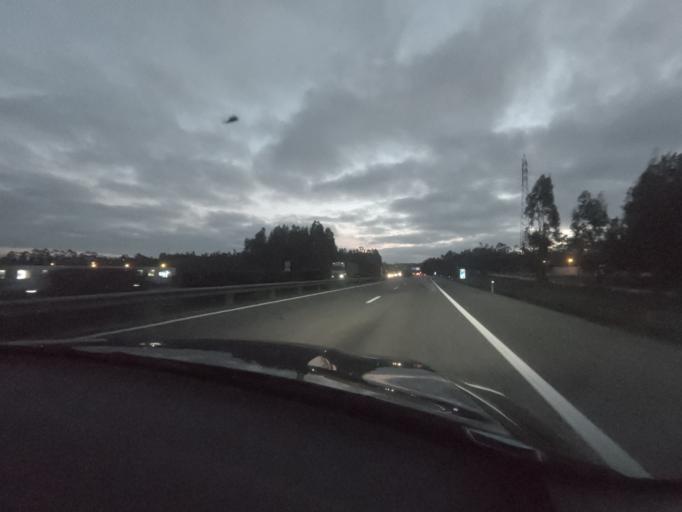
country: PT
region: Leiria
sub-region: Pombal
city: Pombal
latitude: 39.9447
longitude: -8.6738
